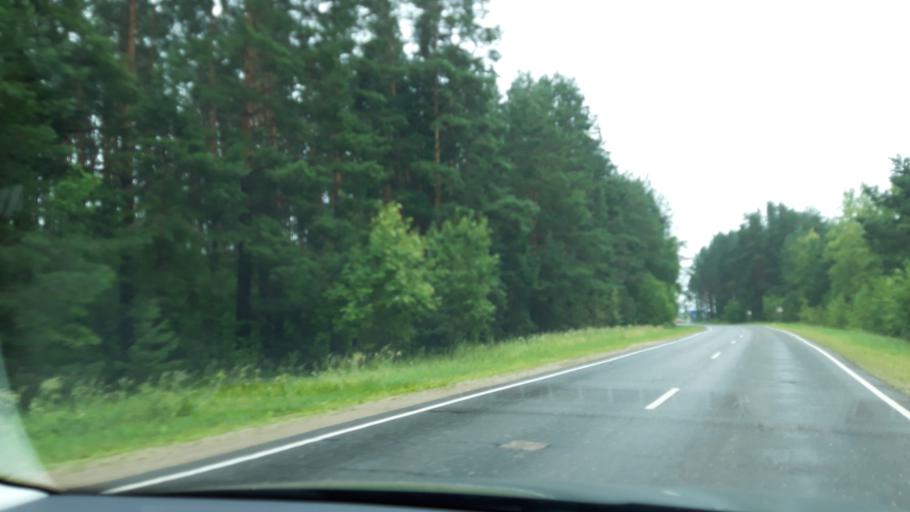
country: RU
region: Tverskaya
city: Zavidovo
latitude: 56.5880
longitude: 36.5404
